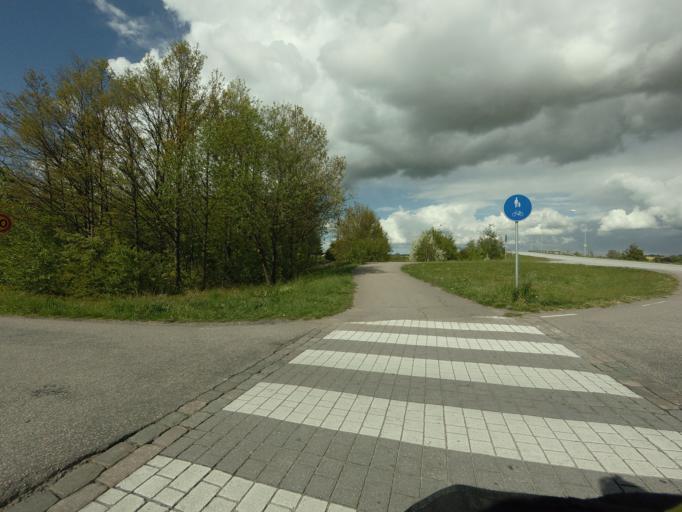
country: SE
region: Skane
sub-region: Landskrona
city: Landskrona
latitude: 55.8919
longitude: 12.8528
